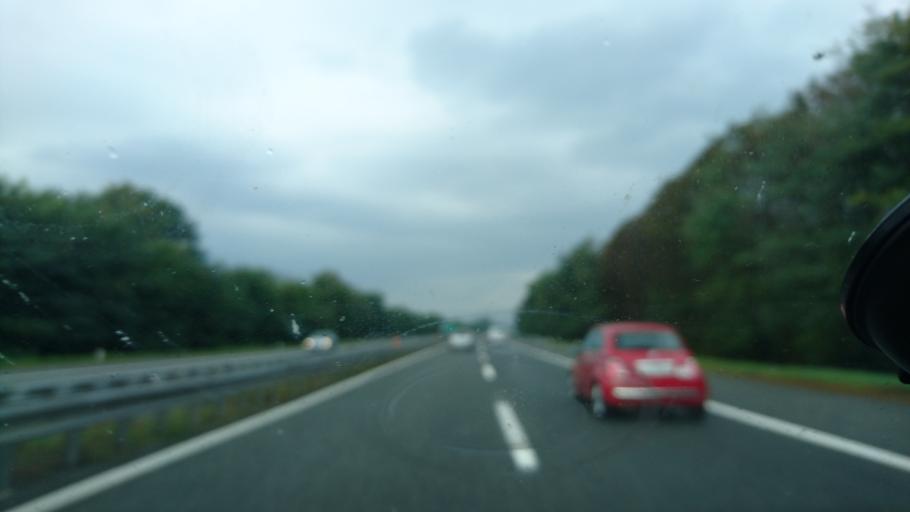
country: IT
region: Piedmont
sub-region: Provincia di Novara
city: Ghemme
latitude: 45.5805
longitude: 8.4066
